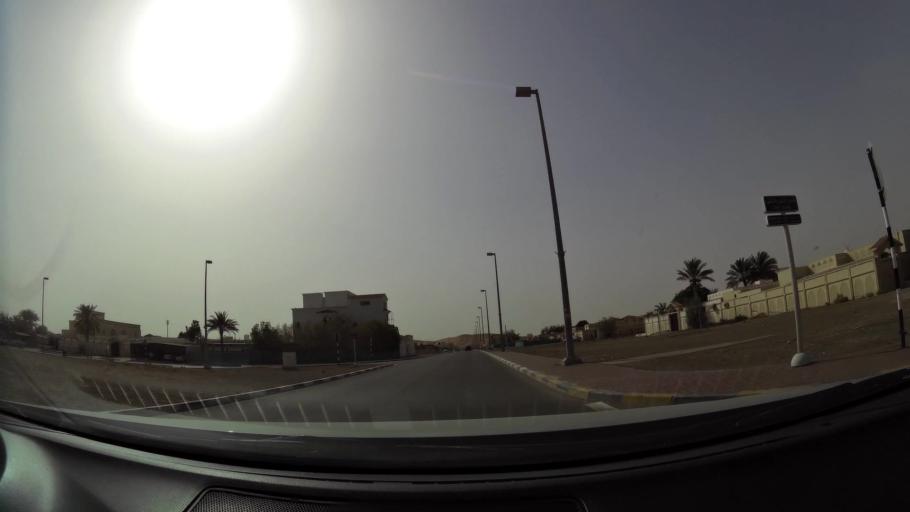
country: AE
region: Abu Dhabi
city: Al Ain
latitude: 24.2108
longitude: 55.5914
